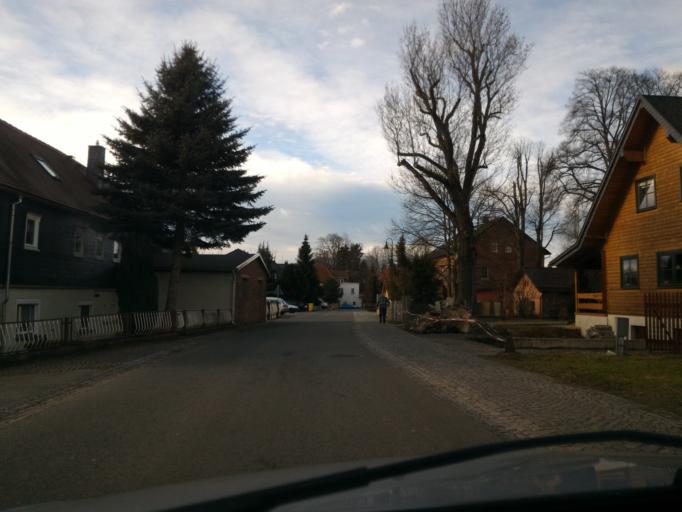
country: DE
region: Saxony
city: Oppach
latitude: 51.0606
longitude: 14.5025
